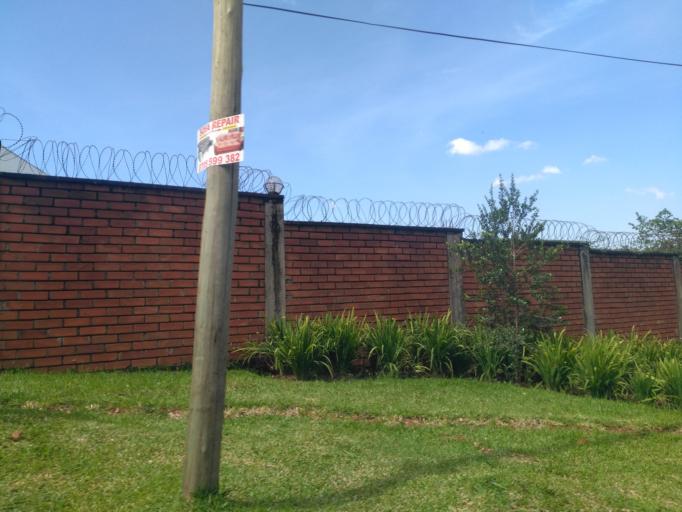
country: UG
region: Central Region
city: Kampala Central Division
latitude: 0.3291
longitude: 32.5773
